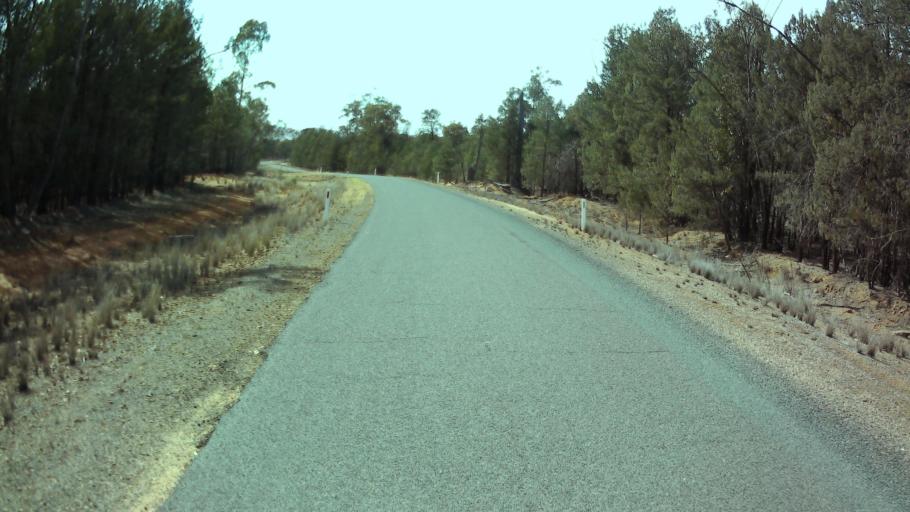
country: AU
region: New South Wales
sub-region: Weddin
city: Grenfell
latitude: -33.7484
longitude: 148.0572
